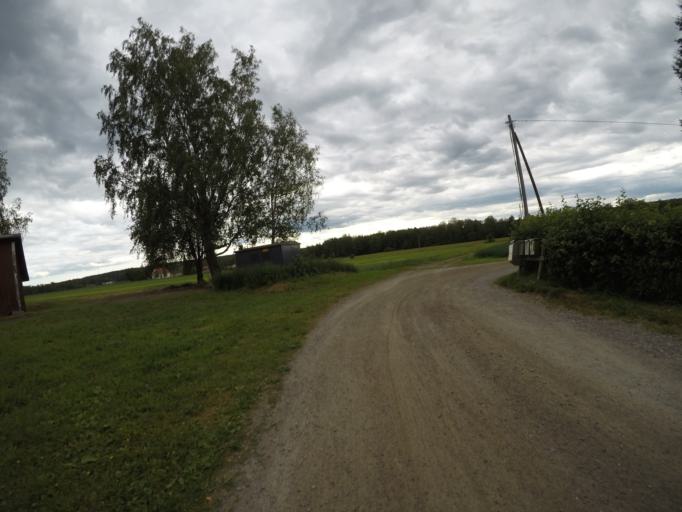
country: FI
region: Haeme
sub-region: Haemeenlinna
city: Haemeenlinna
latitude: 60.9738
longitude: 24.4589
